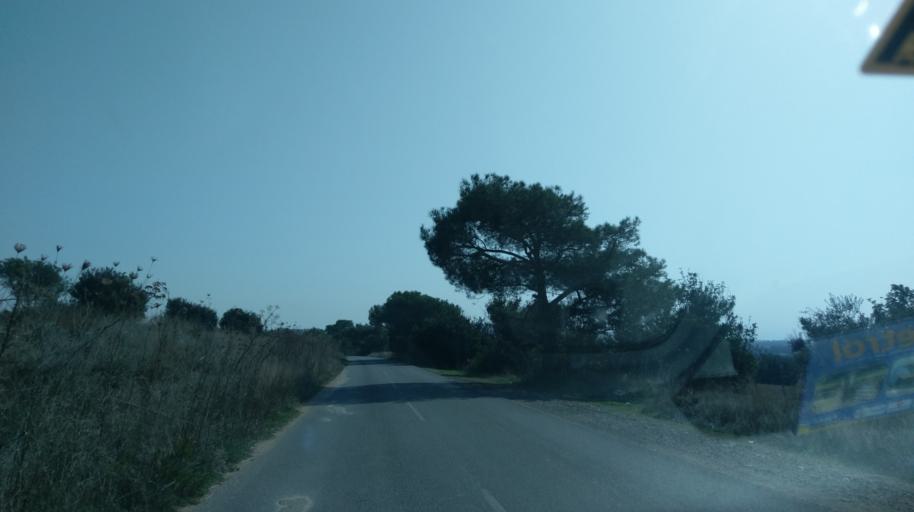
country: CY
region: Lefkosia
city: Morfou
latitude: 35.3320
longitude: 33.0334
